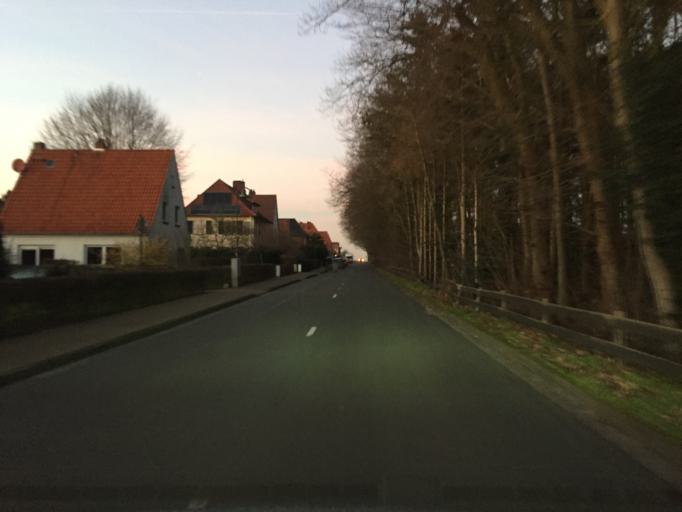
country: DE
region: Lower Saxony
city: Sulingen
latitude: 52.6802
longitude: 8.8141
